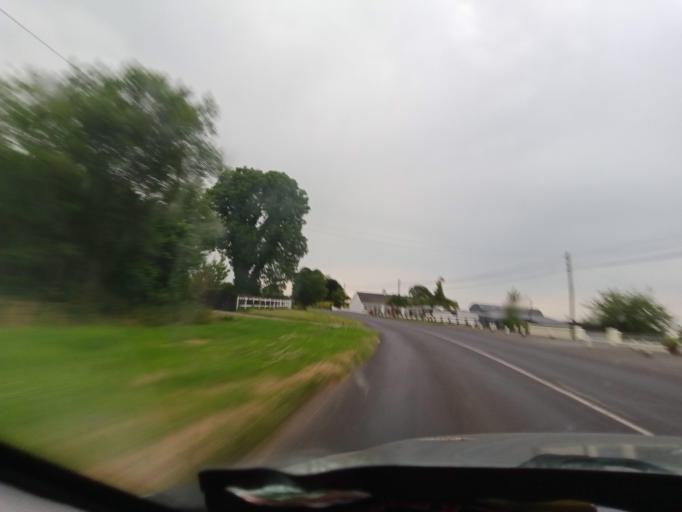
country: IE
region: Leinster
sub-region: Laois
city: Mountmellick
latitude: 53.1423
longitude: -7.4255
